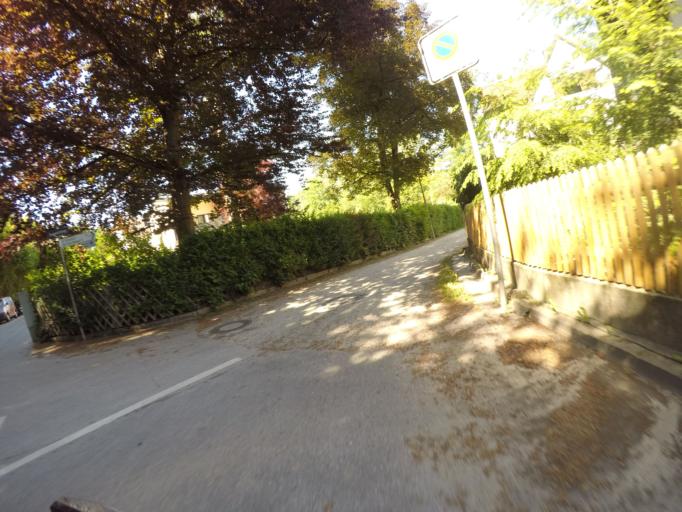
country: DE
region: Bavaria
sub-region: Lower Bavaria
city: Landshut
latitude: 48.5153
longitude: 12.1504
